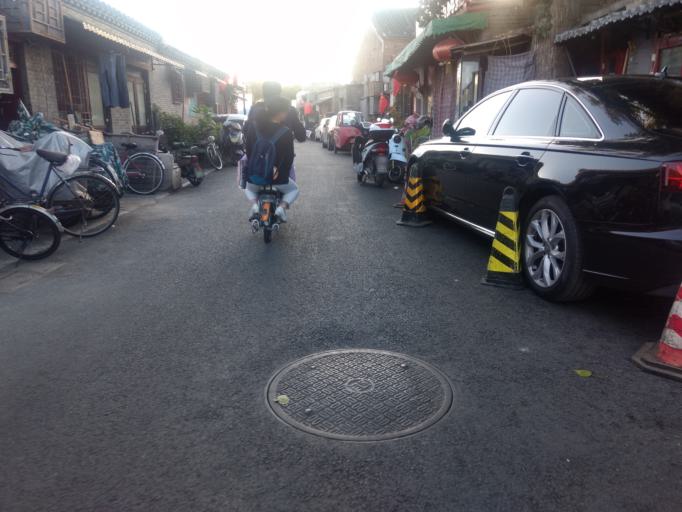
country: CN
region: Beijing
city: Beijing
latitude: 39.8907
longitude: 116.3801
